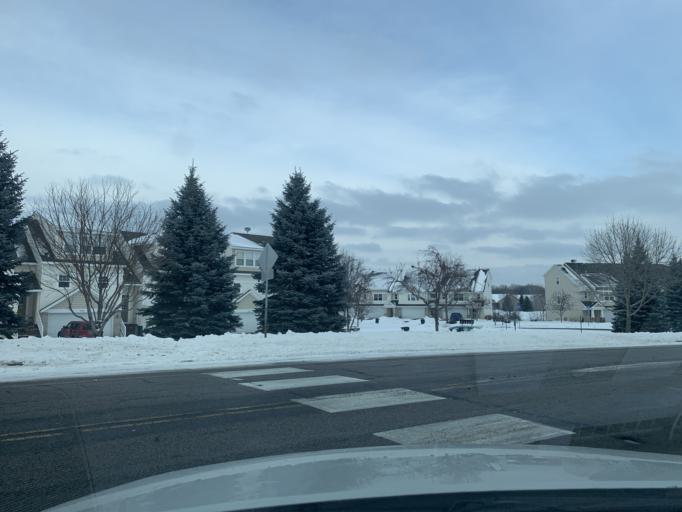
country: US
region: Minnesota
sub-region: Anoka County
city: Ramsey
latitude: 45.2485
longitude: -93.4108
